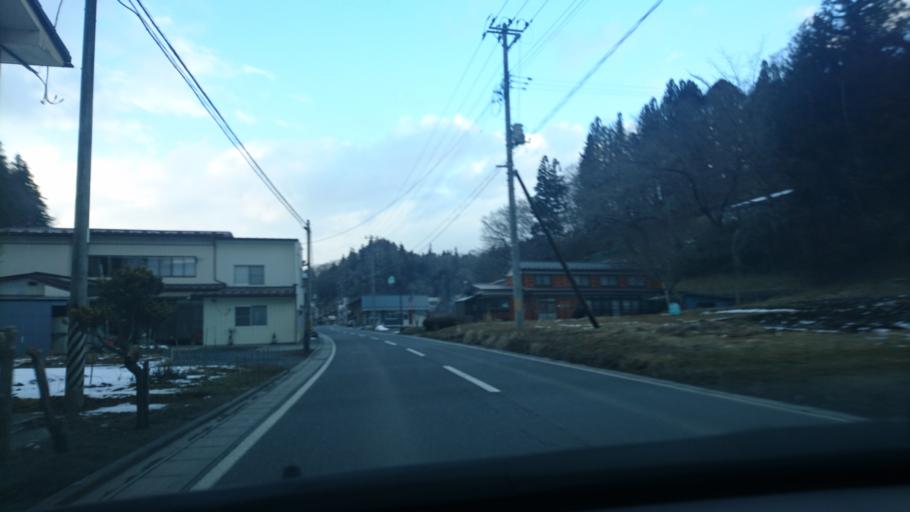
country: JP
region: Iwate
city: Ichinoseki
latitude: 38.9894
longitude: 141.3319
